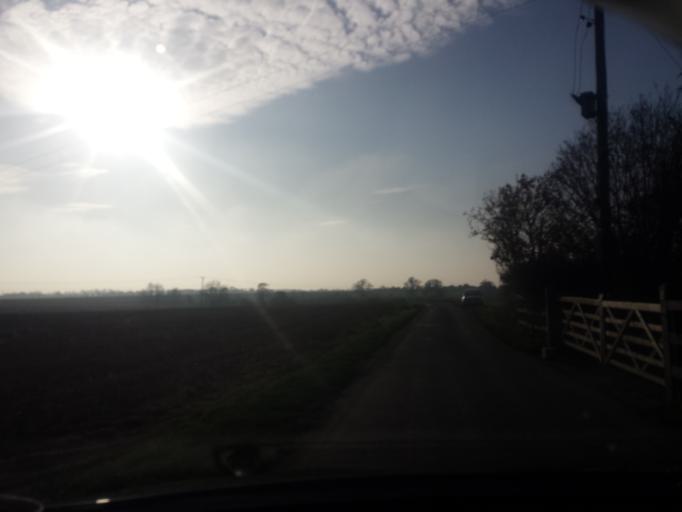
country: GB
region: England
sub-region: Essex
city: Saint Osyth
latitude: 51.8248
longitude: 1.0830
